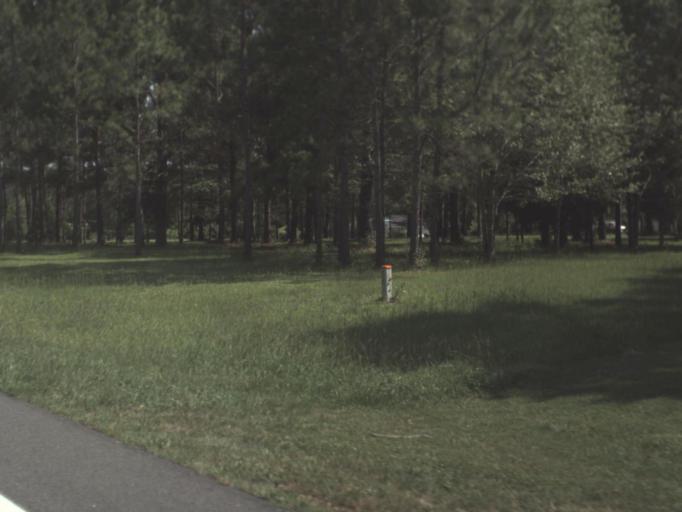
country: US
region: Florida
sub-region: Hamilton County
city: Jasper
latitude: 30.5593
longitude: -82.9835
